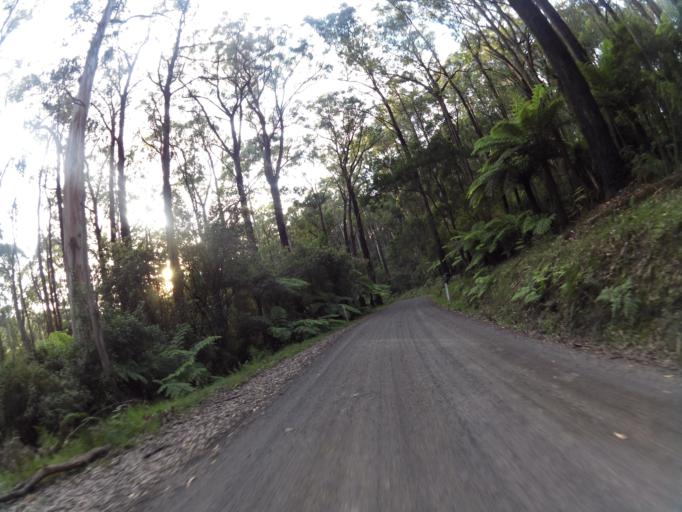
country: AU
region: Victoria
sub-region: Colac-Otway
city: Apollo Bay
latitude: -38.5473
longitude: 143.7366
